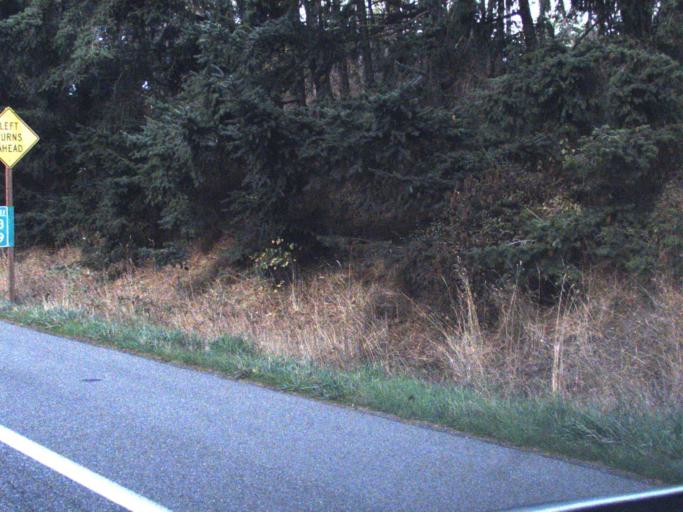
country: US
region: Washington
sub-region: Island County
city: Ault Field
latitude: 48.3659
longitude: -122.6507
